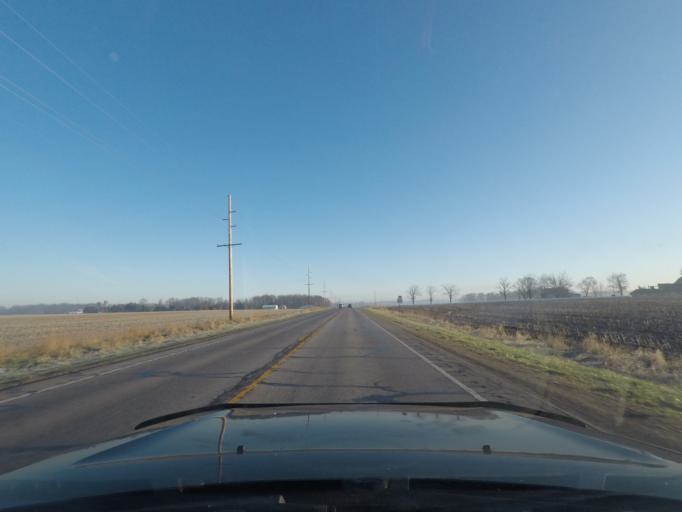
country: US
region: Indiana
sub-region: Elkhart County
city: Wakarusa
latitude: 41.5029
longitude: -86.0020
